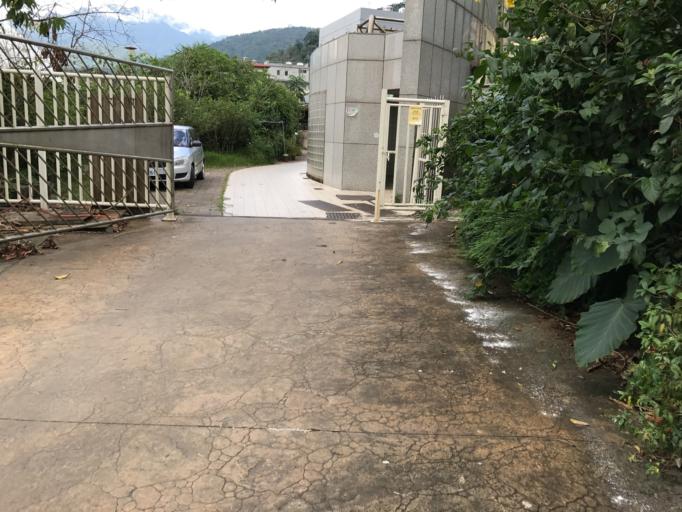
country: TW
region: Taiwan
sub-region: Nantou
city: Puli
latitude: 23.9600
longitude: 120.9992
